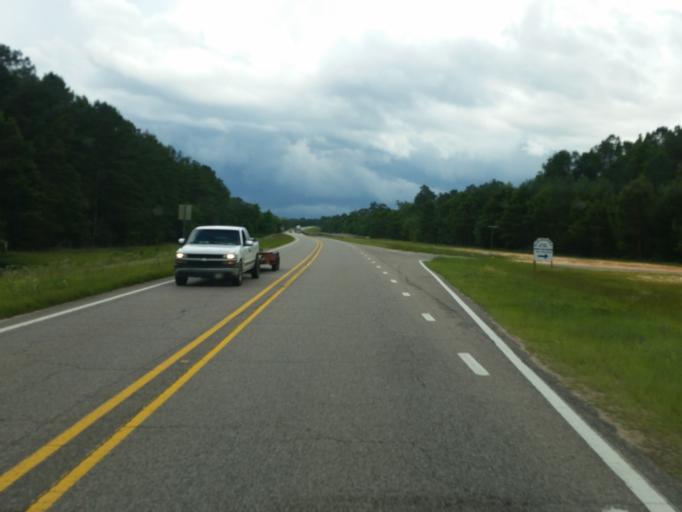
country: US
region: Mississippi
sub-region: George County
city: Lucedale
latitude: 30.8653
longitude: -88.4219
